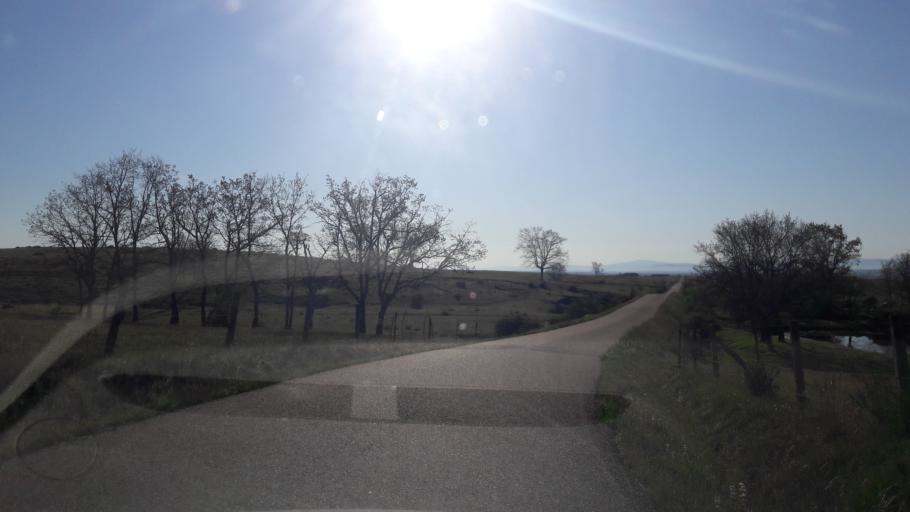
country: ES
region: Castille and Leon
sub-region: Provincia de Salamanca
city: Herguijuela del Campo
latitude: 40.6339
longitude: -5.8860
